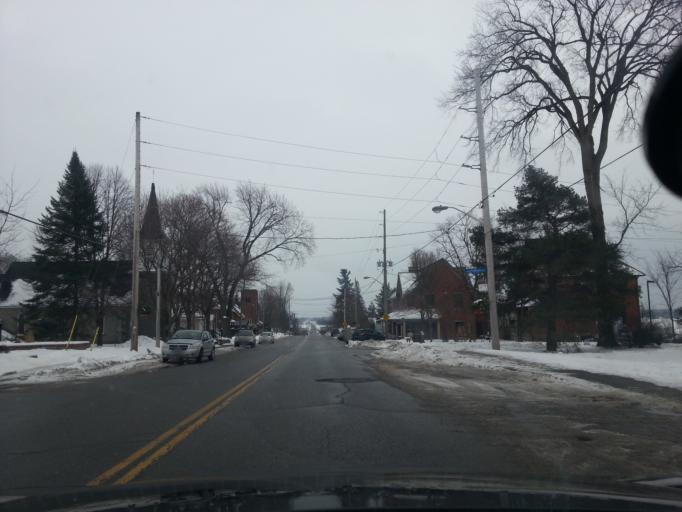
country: CA
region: Ontario
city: Bells Corners
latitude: 45.3465
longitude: -76.0383
